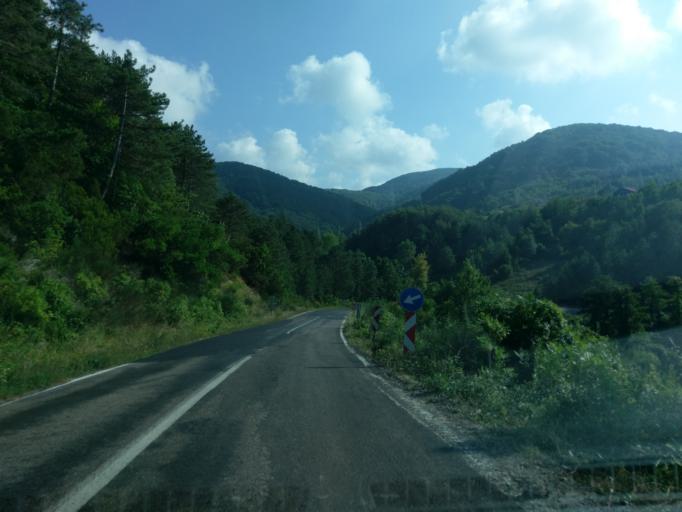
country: TR
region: Sinop
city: Yenikonak
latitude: 41.9416
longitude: 34.7073
